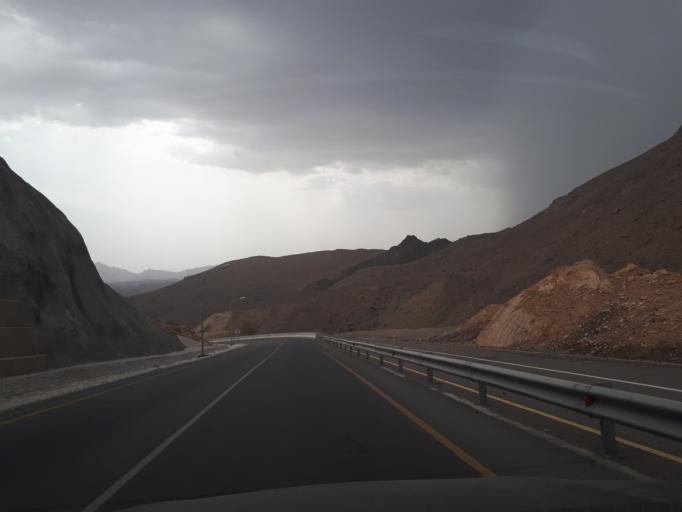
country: OM
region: Ash Sharqiyah
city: Badiyah
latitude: 22.5723
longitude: 59.0708
